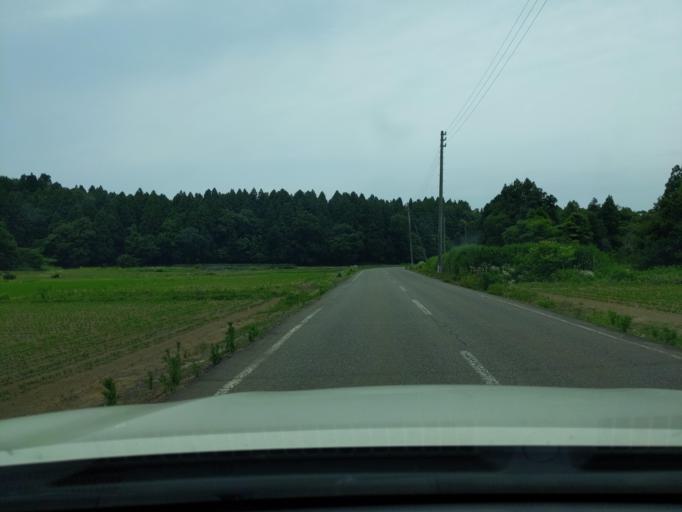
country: JP
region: Niigata
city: Kashiwazaki
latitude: 37.3336
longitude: 138.5562
